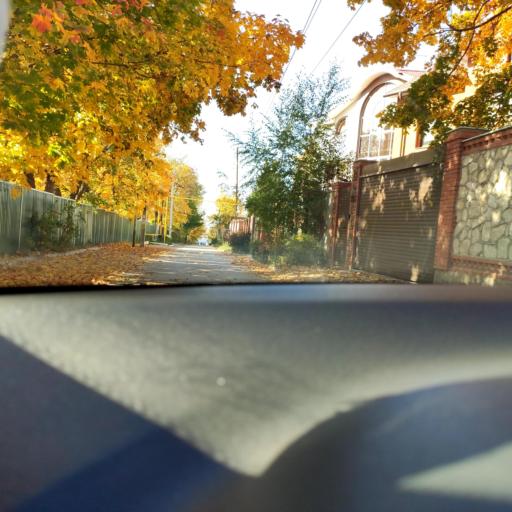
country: RU
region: Samara
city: Samara
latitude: 53.2664
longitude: 50.1895
